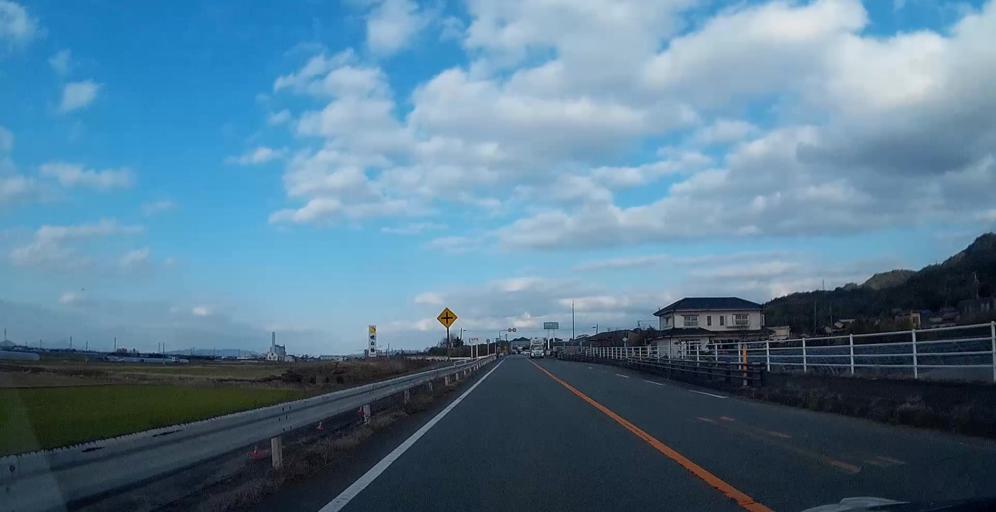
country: JP
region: Kumamoto
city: Yatsushiro
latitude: 32.5353
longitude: 130.6679
